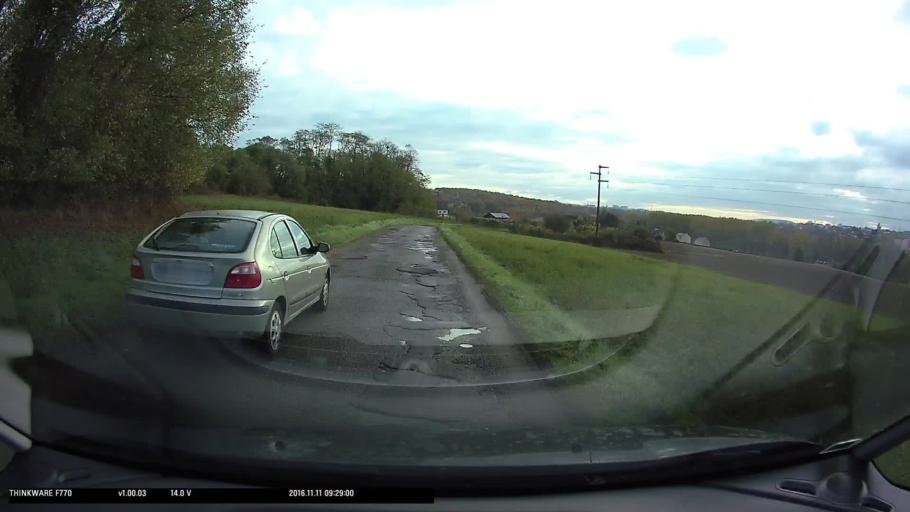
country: FR
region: Ile-de-France
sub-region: Departement du Val-d'Oise
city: Osny
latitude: 49.0700
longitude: 2.0459
